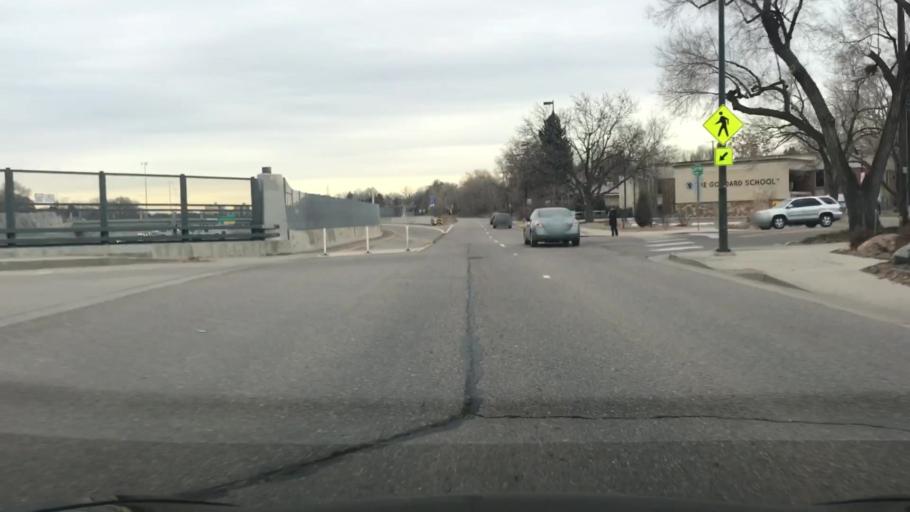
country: US
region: Colorado
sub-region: Arapahoe County
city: Englewood
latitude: 39.6917
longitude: -104.9772
